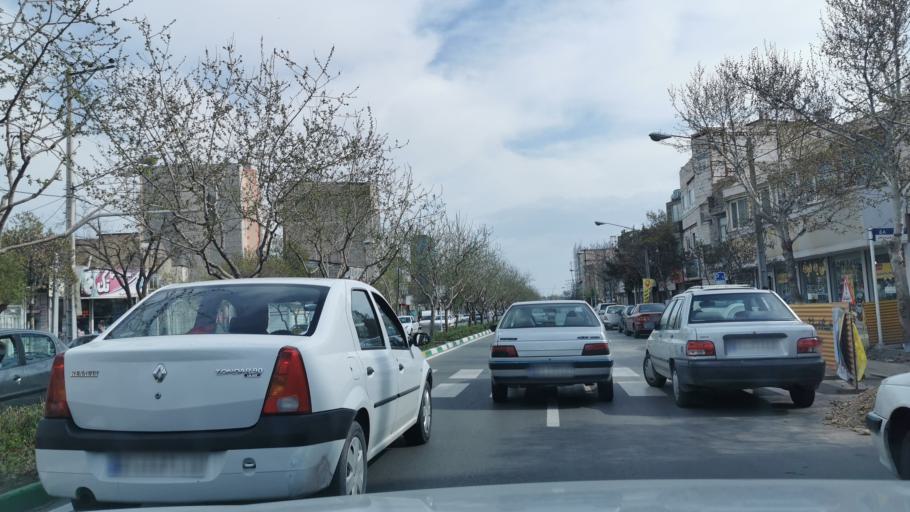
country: IR
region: Razavi Khorasan
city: Mashhad
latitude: 36.3140
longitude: 59.6118
